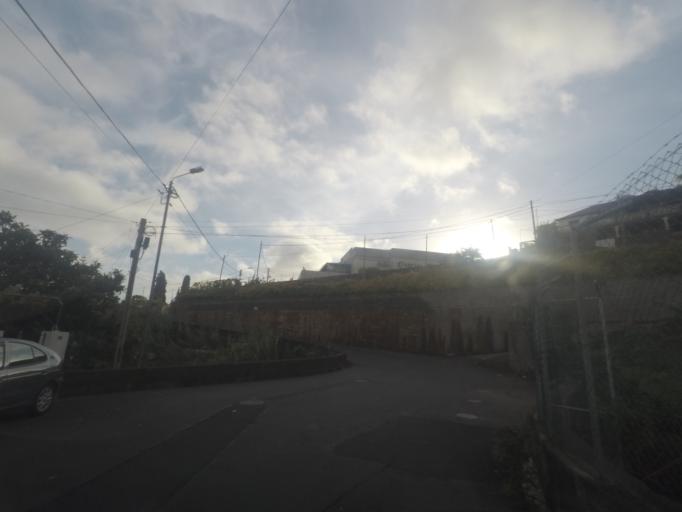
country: PT
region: Madeira
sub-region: Funchal
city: Nossa Senhora do Monte
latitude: 32.6699
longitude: -16.9395
